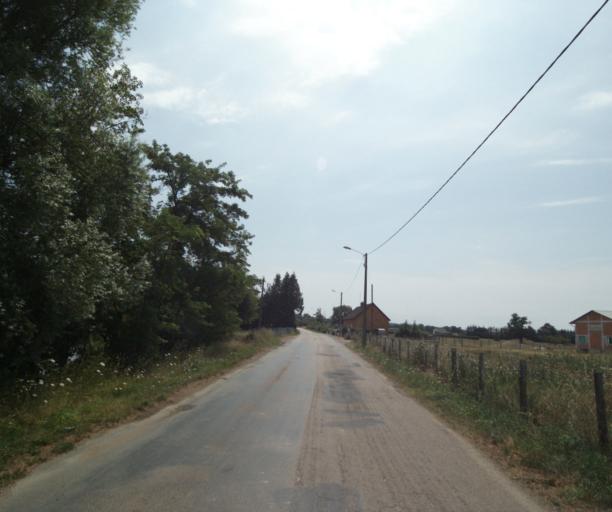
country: FR
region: Bourgogne
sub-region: Departement de Saone-et-Loire
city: Gueugnon
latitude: 46.5931
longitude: 4.0524
